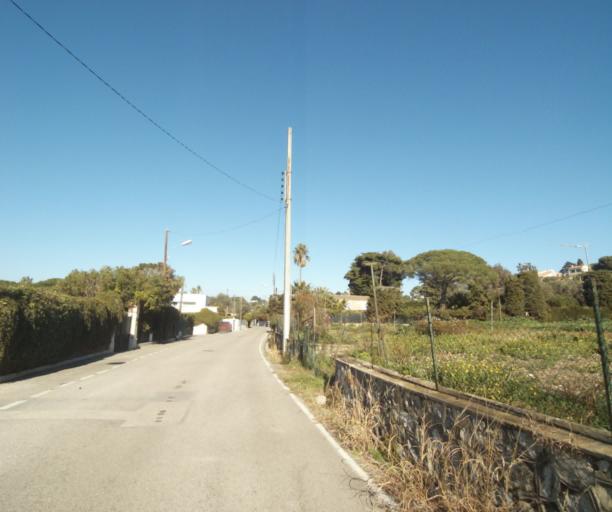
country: FR
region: Provence-Alpes-Cote d'Azur
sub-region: Departement des Alpes-Maritimes
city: Antibes
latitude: 43.5562
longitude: 7.1249
